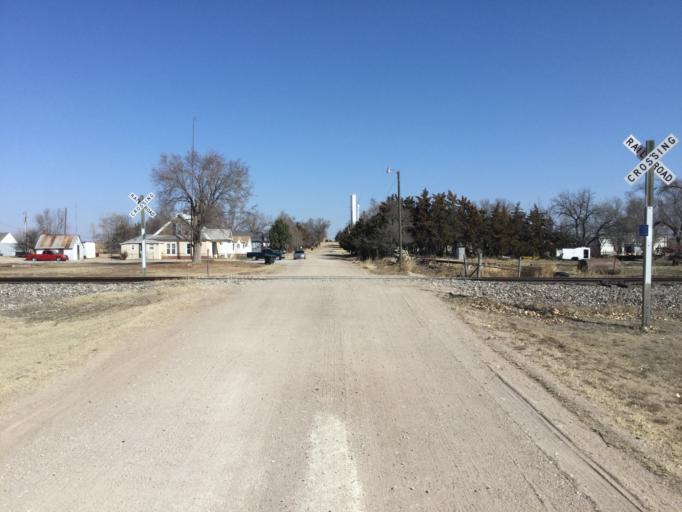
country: US
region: Kansas
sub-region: Rush County
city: La Crosse
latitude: 38.4668
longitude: -99.3102
